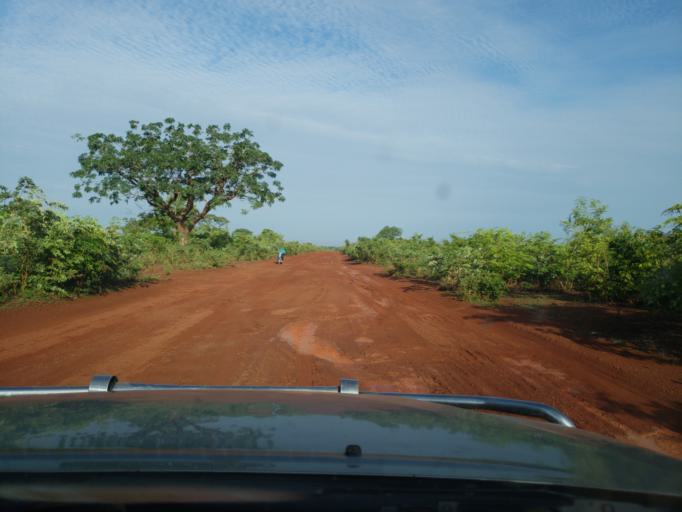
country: ML
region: Sikasso
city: Koutiala
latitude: 12.4265
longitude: -5.6410
